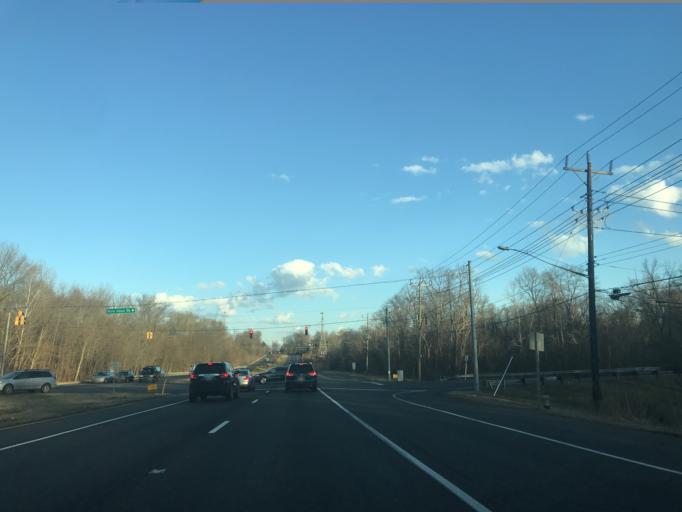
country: US
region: Maryland
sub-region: Prince George's County
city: Kettering
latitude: 38.8762
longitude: -76.8036
